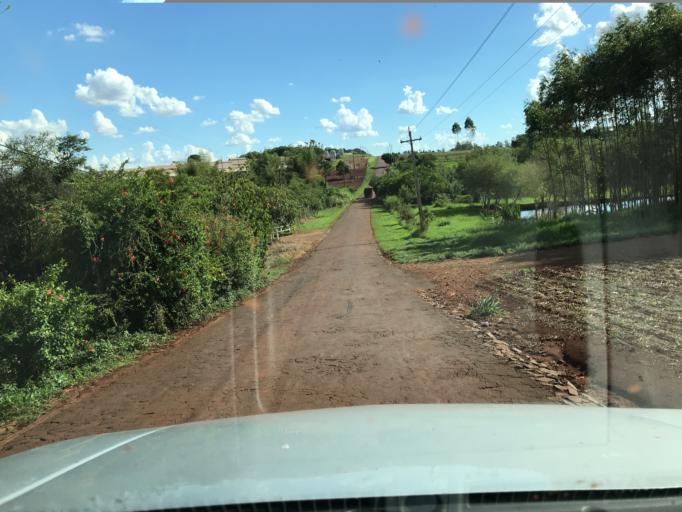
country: BR
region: Parana
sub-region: Palotina
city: Palotina
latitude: -24.2560
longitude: -53.7970
